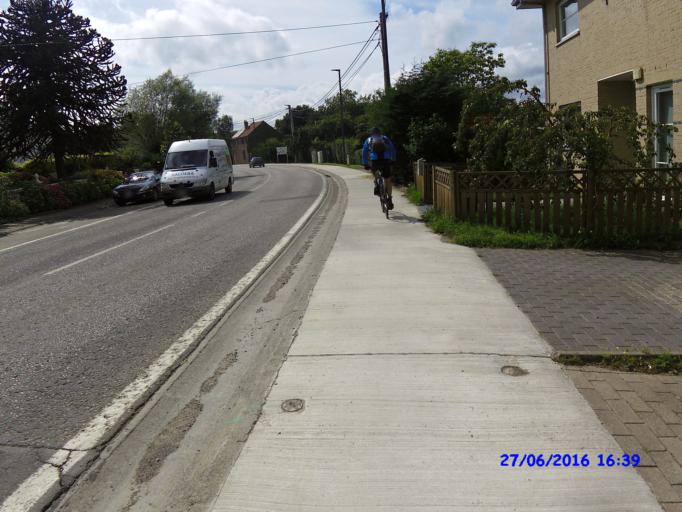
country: BE
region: Flanders
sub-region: Provincie Vlaams-Brabant
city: Dilbeek
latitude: 50.8174
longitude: 4.2566
